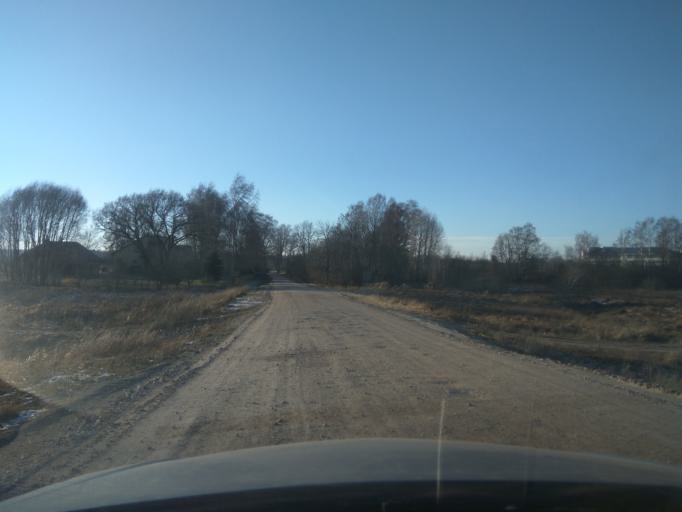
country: LV
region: Kuldigas Rajons
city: Kuldiga
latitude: 56.9609
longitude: 21.9623
